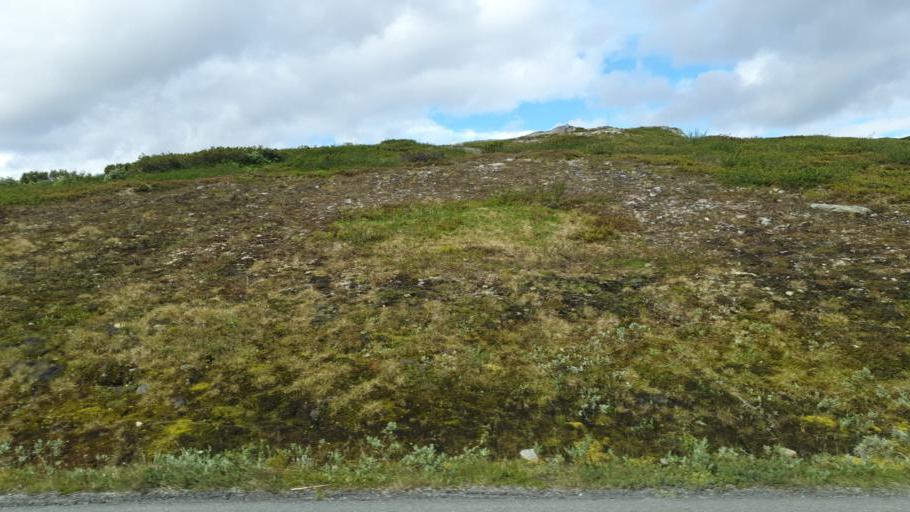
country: NO
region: Oppland
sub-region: Vestre Slidre
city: Slidre
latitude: 61.3176
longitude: 8.8073
